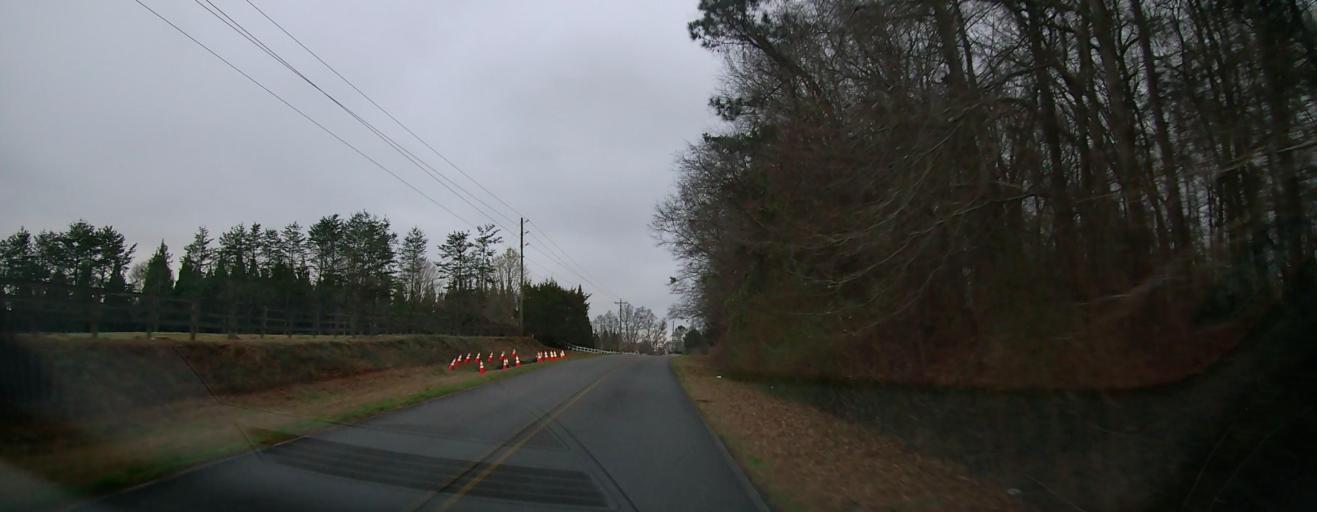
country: US
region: Georgia
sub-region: Lamar County
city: Barnesville
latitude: 33.0250
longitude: -84.1128
